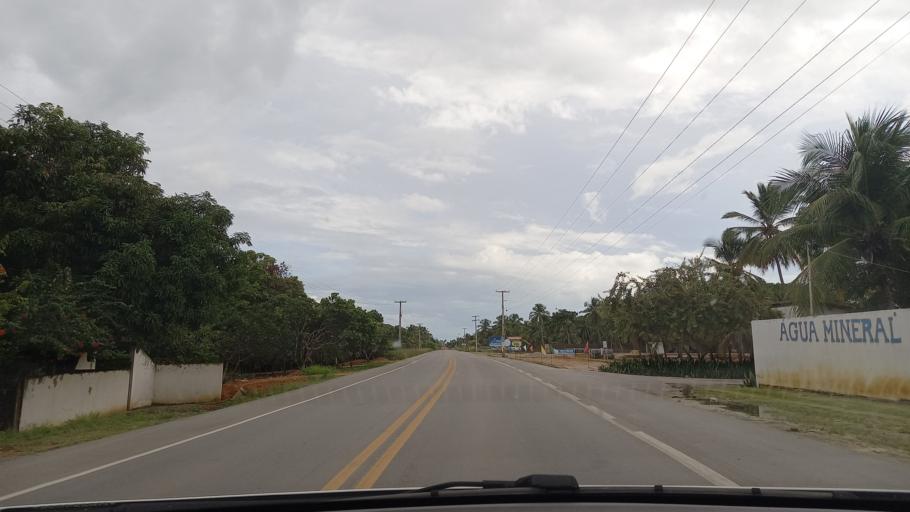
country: BR
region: Alagoas
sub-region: Maragogi
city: Maragogi
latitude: -8.9602
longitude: -35.1799
